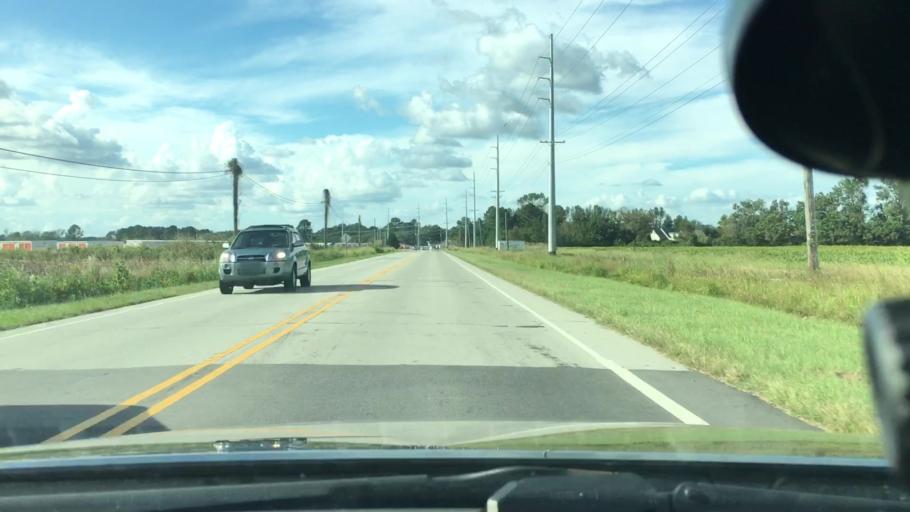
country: US
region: North Carolina
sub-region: Pitt County
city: Windsor
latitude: 35.5518
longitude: -77.3269
